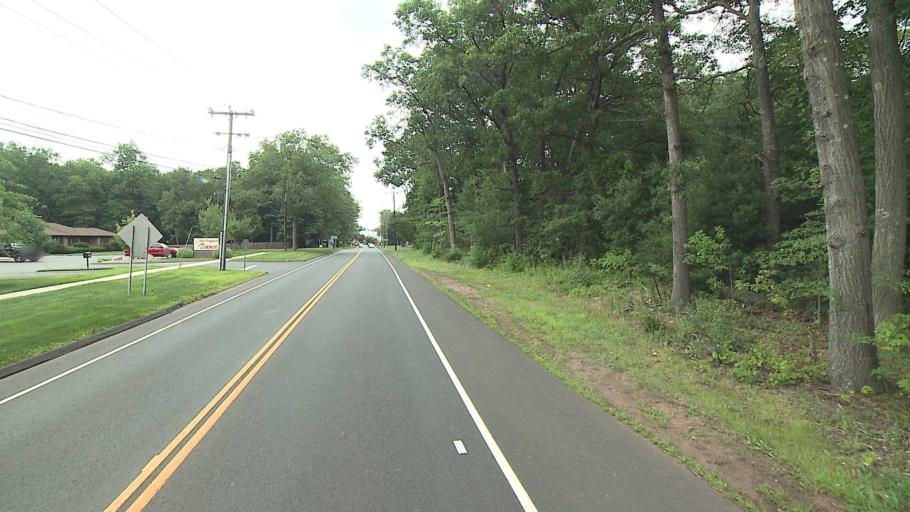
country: US
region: Connecticut
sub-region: Middlesex County
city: Cromwell
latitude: 41.6318
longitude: -72.6763
